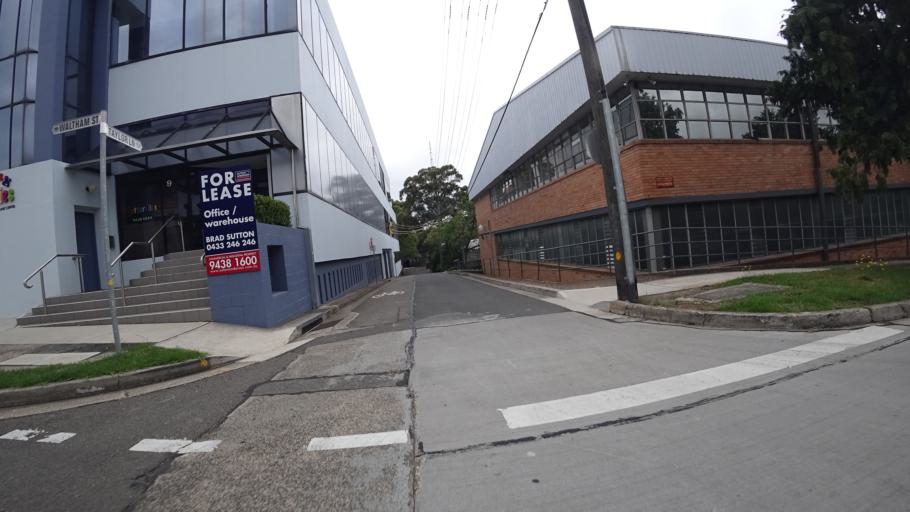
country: AU
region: New South Wales
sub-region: Willoughby
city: Artarmon
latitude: -33.8149
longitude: 151.1880
